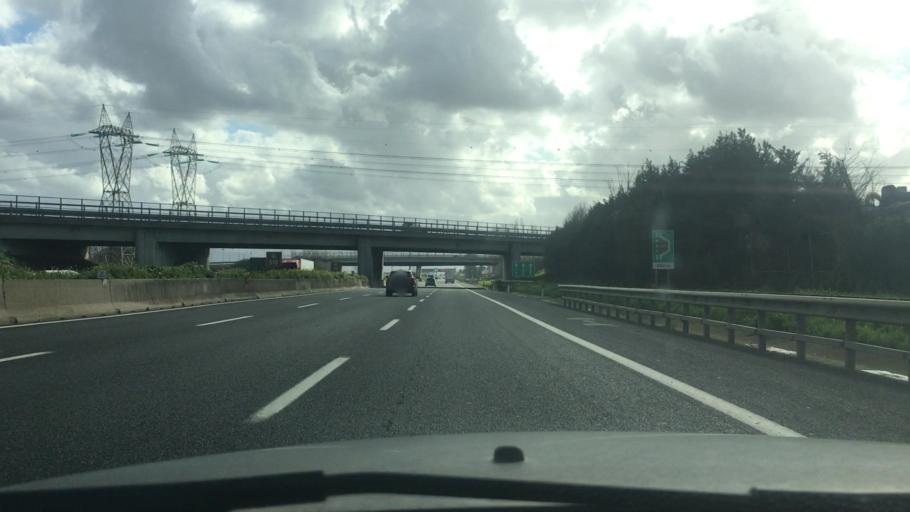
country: IT
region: Campania
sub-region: Provincia di Caserta
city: San Marco Evangelista
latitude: 41.0134
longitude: 14.3226
